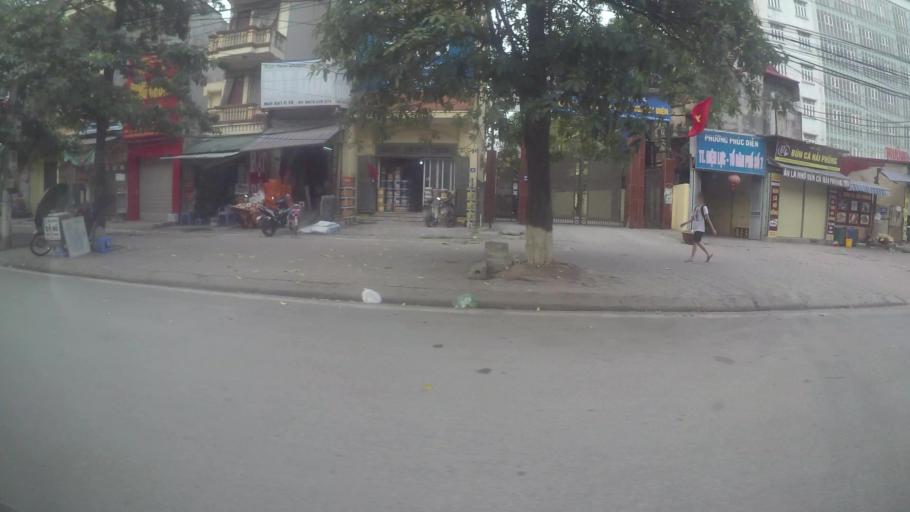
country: VN
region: Ha Noi
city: Cau Dien
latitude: 21.0457
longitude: 105.7511
